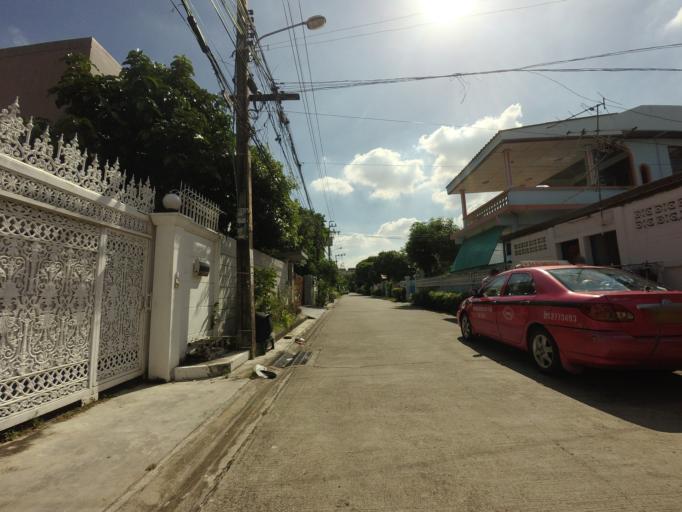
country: TH
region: Bangkok
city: Lat Phrao
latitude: 13.7945
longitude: 100.5919
